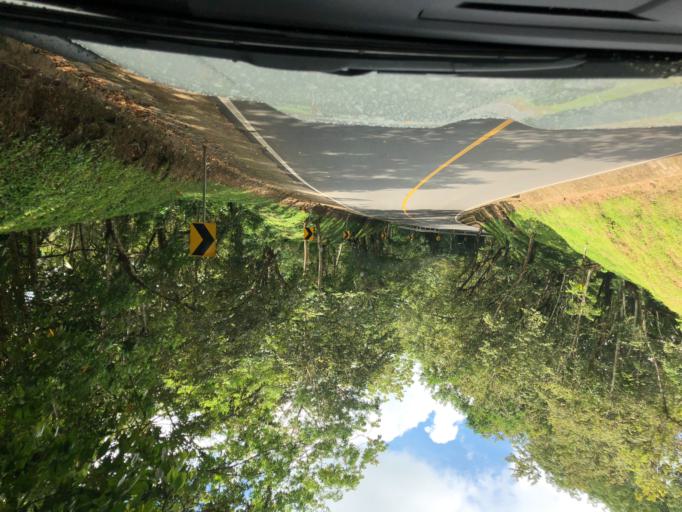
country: NI
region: Chontales
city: Villa Sandino
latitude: 11.9947
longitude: -84.9127
